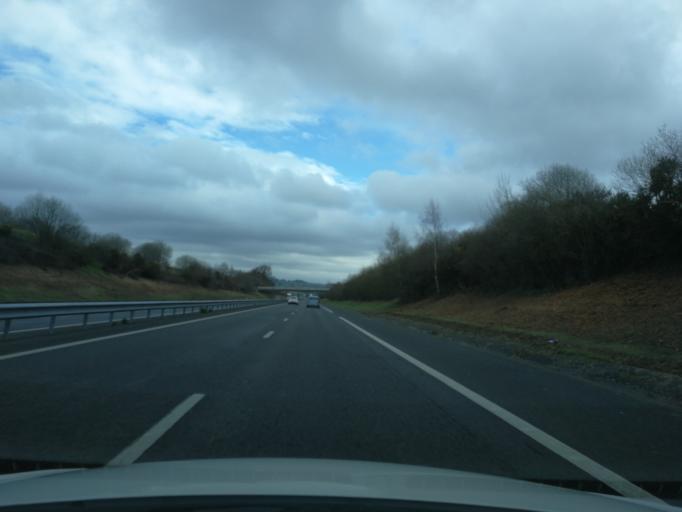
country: FR
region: Brittany
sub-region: Departement d'Ille-et-Vilaine
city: Saint-Jean-sur-Couesnon
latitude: 48.2896
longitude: -1.3784
